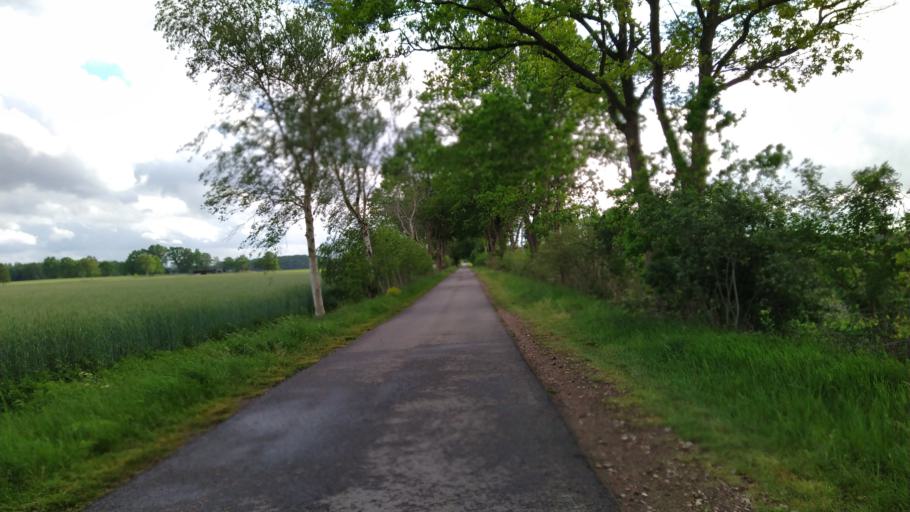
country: DE
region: Lower Saxony
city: Brest
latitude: 53.4431
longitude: 9.3655
